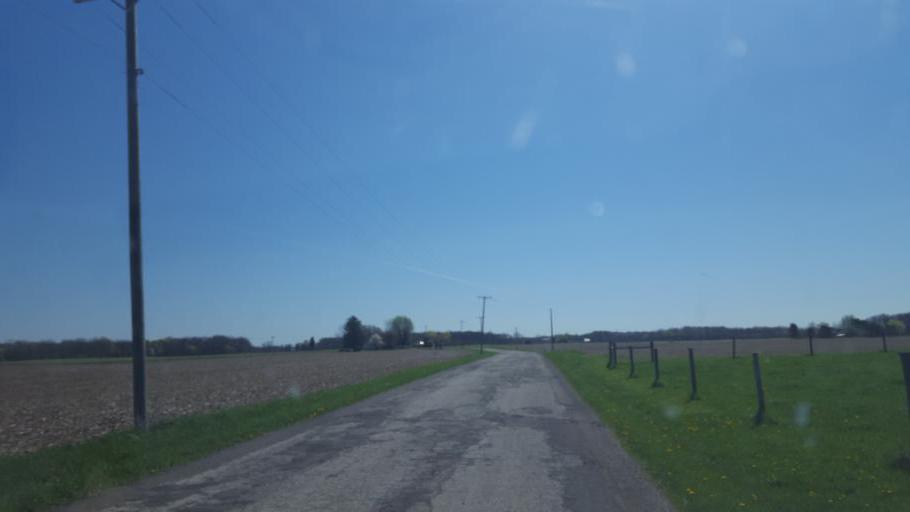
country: US
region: Ohio
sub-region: Morrow County
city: Mount Gilead
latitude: 40.6114
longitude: -82.8659
